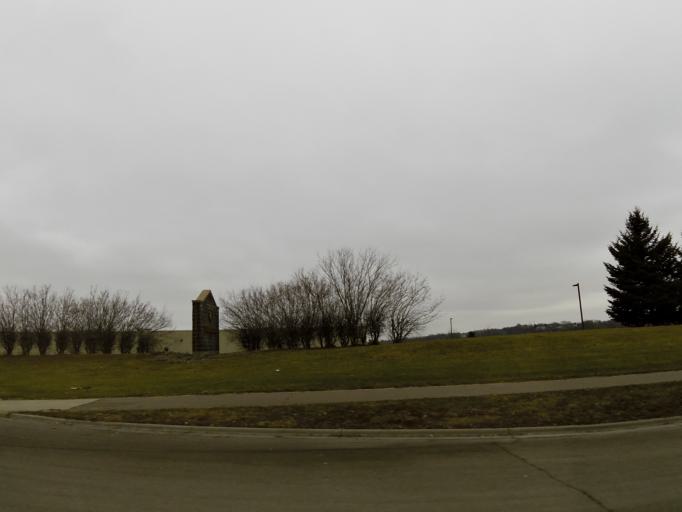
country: US
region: Minnesota
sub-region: Scott County
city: Savage
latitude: 44.7465
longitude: -93.3270
